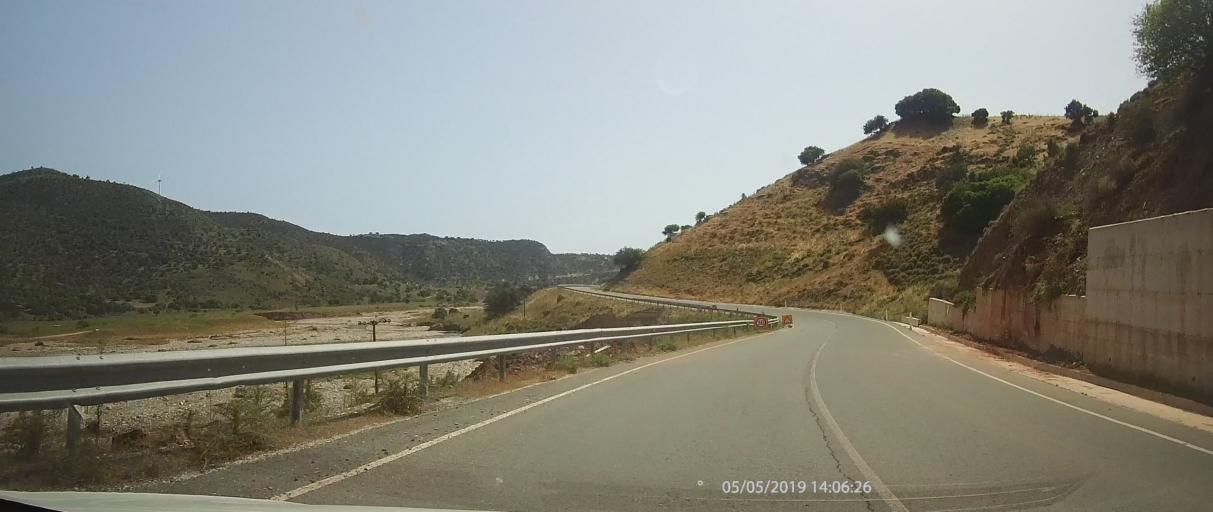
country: CY
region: Limassol
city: Pissouri
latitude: 34.7453
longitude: 32.6074
